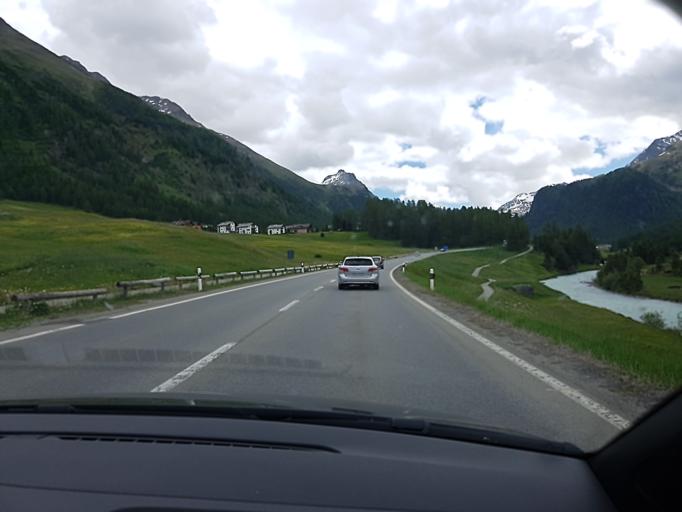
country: CH
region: Grisons
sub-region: Maloja District
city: Pontresina
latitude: 46.5079
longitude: 9.8835
